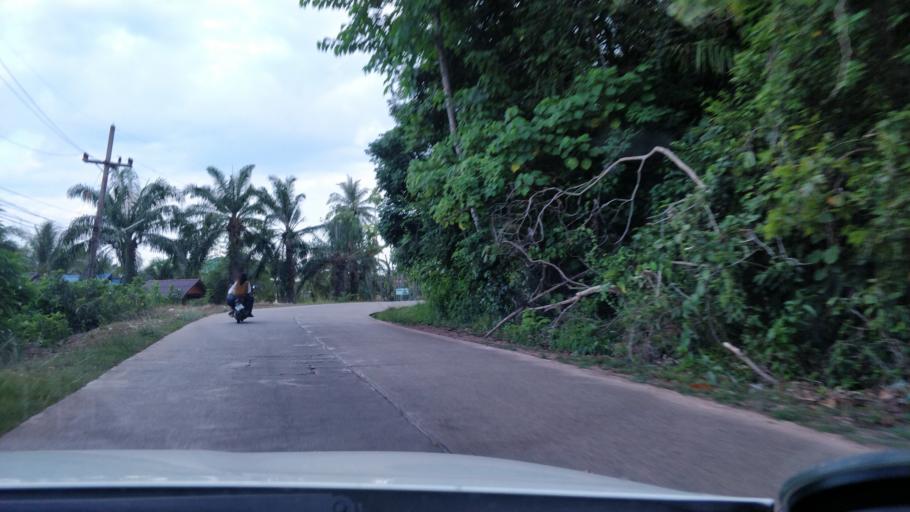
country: TH
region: Krabi
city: Saladan
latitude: 7.5785
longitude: 99.0681
